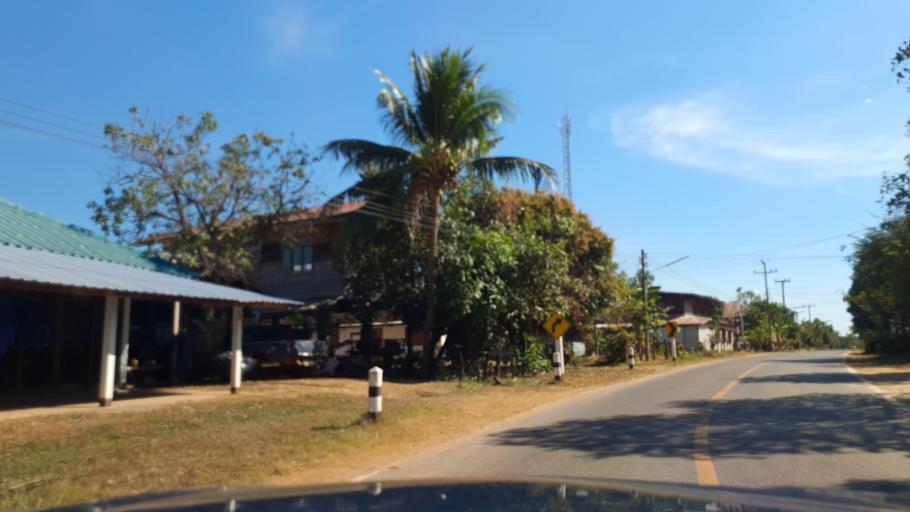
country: TH
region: Kalasin
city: Khao Wong
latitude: 16.7159
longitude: 104.1144
